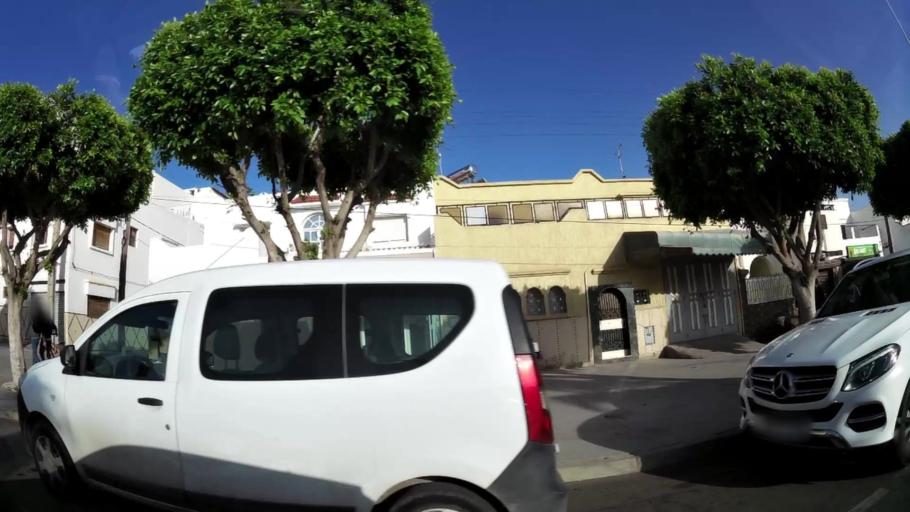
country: MA
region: Oued ed Dahab-Lagouira
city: Dakhla
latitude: 30.4087
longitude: -9.5494
